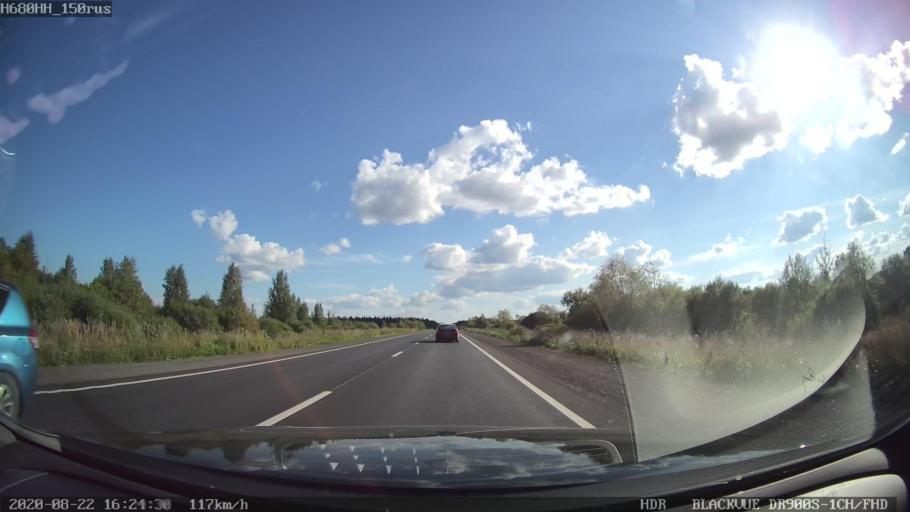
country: RU
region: Tverskaya
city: Rameshki
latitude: 57.3362
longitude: 36.0948
